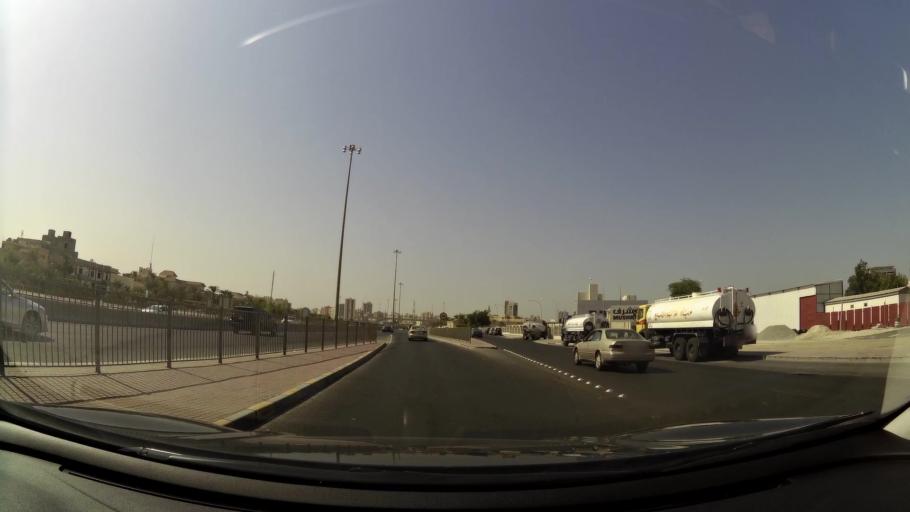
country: KW
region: Muhafazat Hawalli
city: As Salimiyah
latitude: 29.3252
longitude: 48.0831
